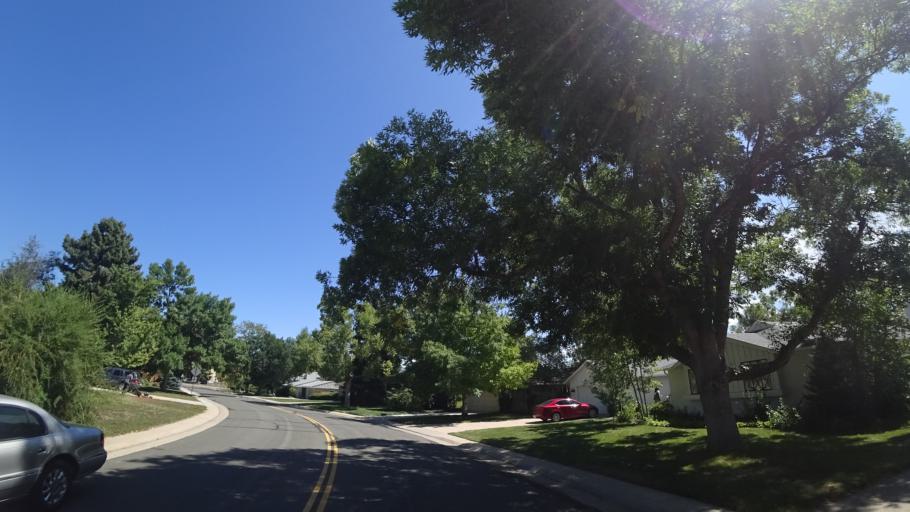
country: US
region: Colorado
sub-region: Arapahoe County
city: Greenwood Village
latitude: 39.6081
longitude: -104.9617
